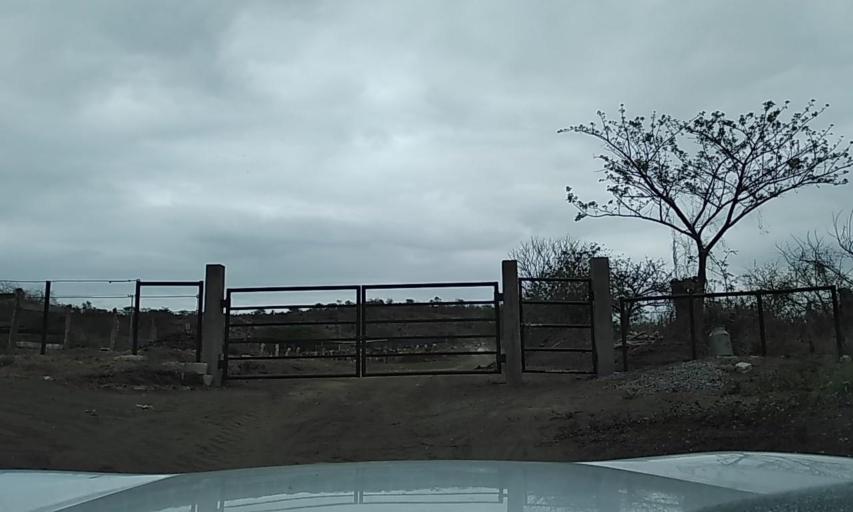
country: MX
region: Veracruz
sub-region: Veracruz
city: Delfino Victoria (Santa Fe)
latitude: 19.2703
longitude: -96.3070
